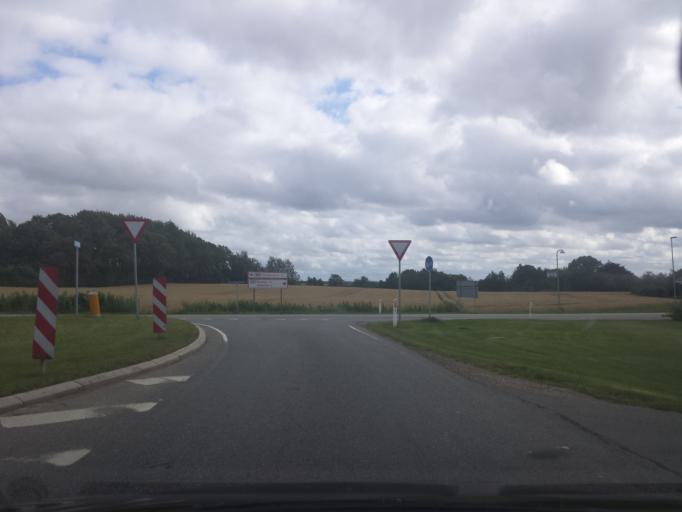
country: DK
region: South Denmark
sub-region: Sonderborg Kommune
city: Grasten
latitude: 54.9397
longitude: 9.6277
